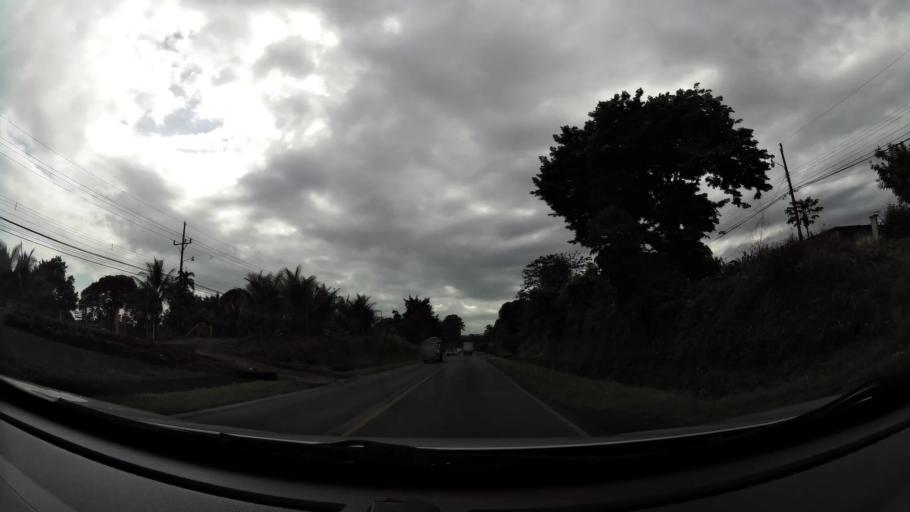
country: CR
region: Limon
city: Pocora
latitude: 10.1647
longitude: -83.6027
